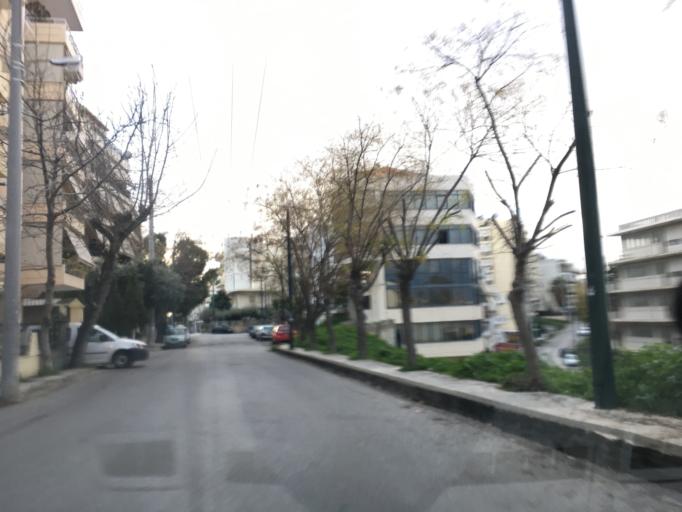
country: GR
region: Attica
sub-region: Nomarchia Athinas
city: Nea Filadelfeia
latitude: 38.0534
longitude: 23.7432
